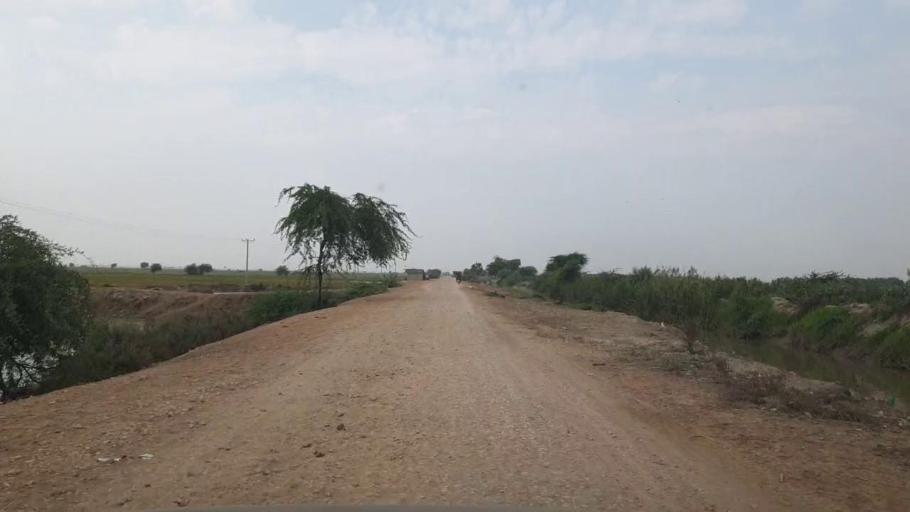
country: PK
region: Sindh
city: Kario
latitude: 24.6081
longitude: 68.5950
